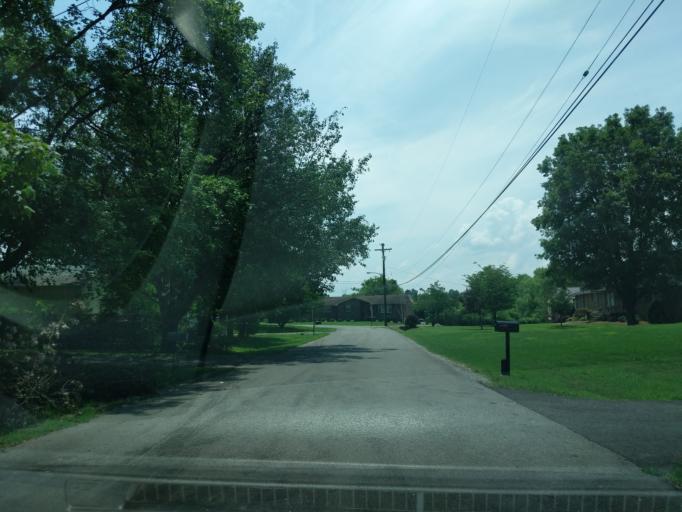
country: US
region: Tennessee
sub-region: Davidson County
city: Lakewood
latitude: 36.2429
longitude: -86.6454
